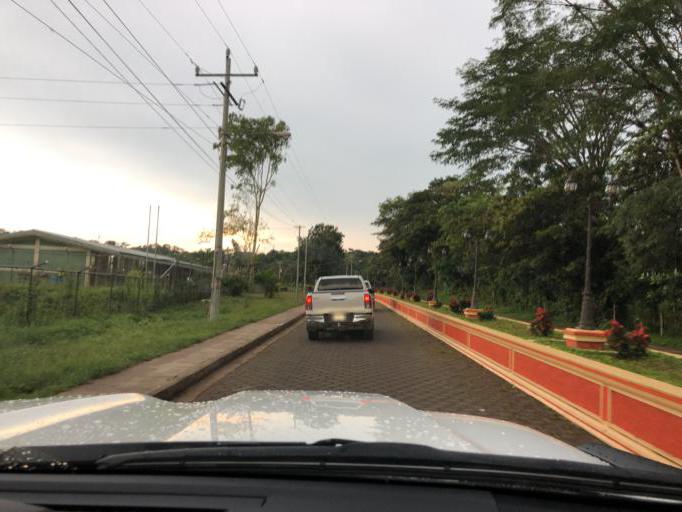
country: NI
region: Chontales
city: La Libertad
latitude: 12.2107
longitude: -85.1683
